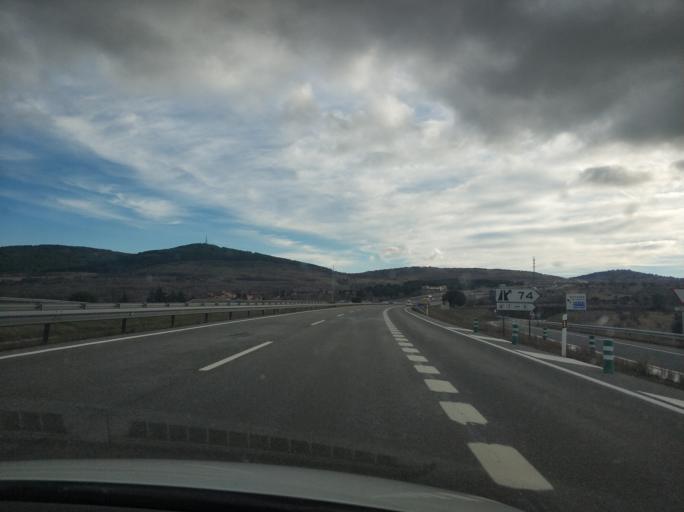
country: ES
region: Madrid
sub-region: Provincia de Madrid
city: Buitrago del Lozoya
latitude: 40.9832
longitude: -3.6396
